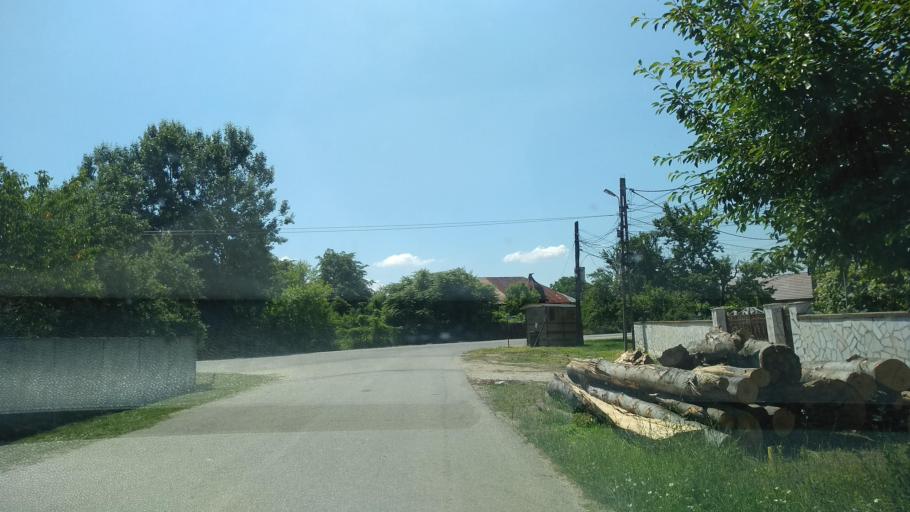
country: RO
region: Gorj
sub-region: Comuna Turcinesti
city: Turcinesti
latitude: 45.1097
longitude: 23.3178
